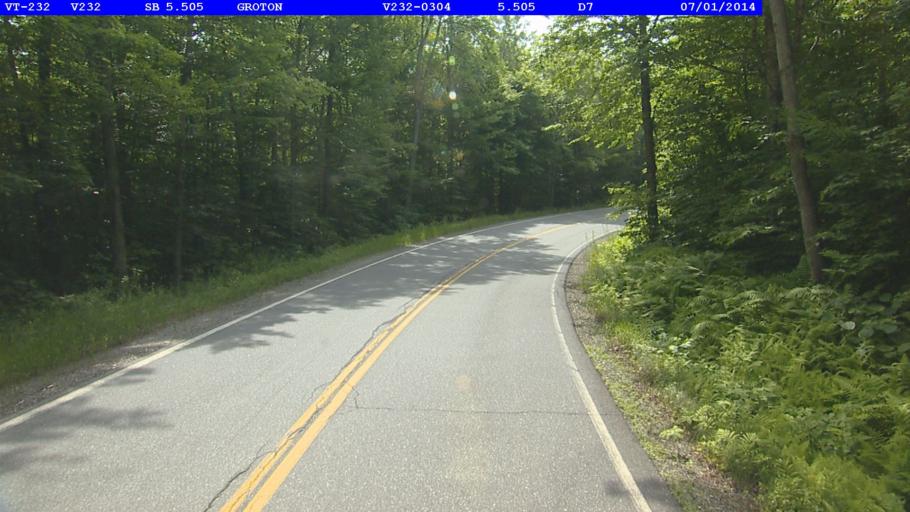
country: US
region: Vermont
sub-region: Washington County
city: Barre
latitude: 44.2786
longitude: -72.2858
